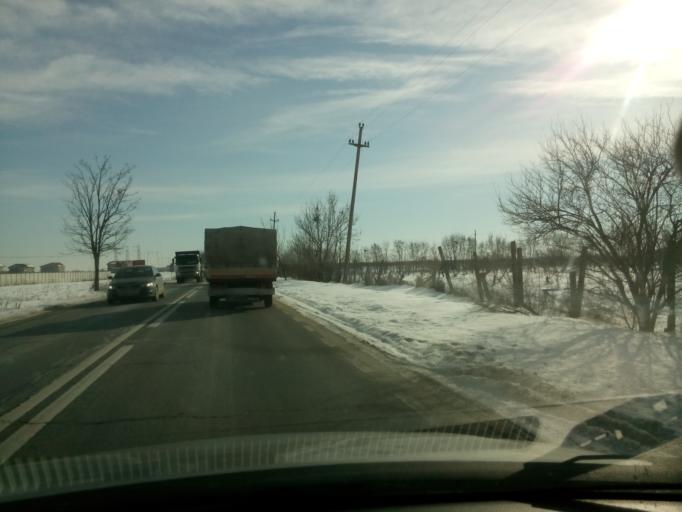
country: RO
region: Ilfov
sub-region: Comuna Glina
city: Glina
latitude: 44.3261
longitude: 26.2595
